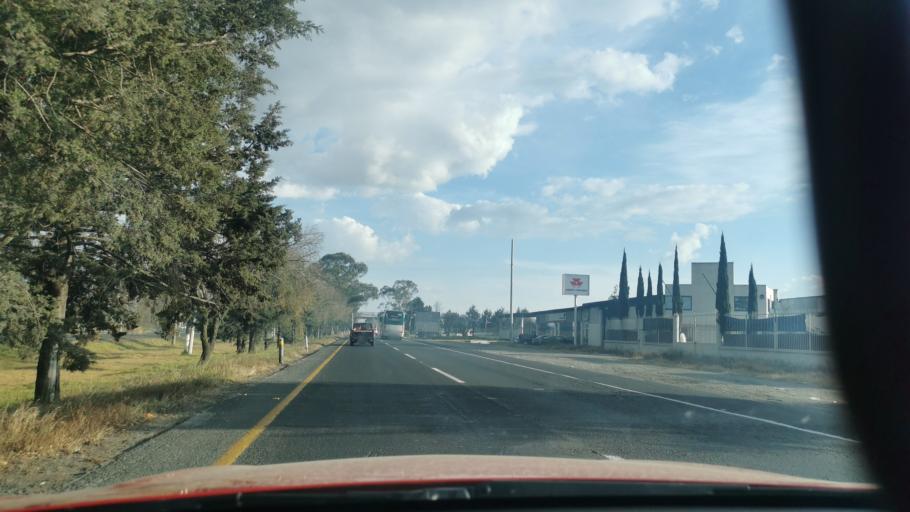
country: MX
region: Mexico
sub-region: Toluca
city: Colonia Aviacion Autopan
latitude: 19.3776
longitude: -99.7018
